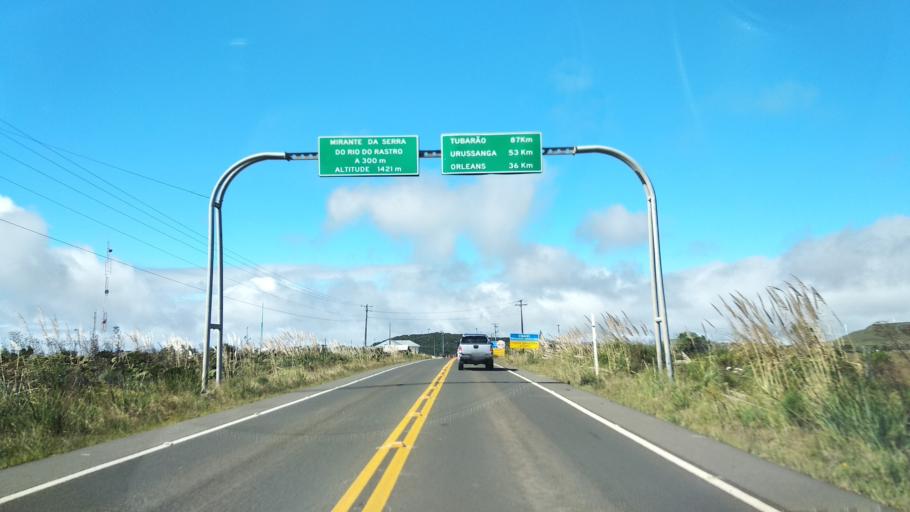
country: BR
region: Santa Catarina
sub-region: Lauro Muller
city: Lauro Muller
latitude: -28.3915
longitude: -49.5511
